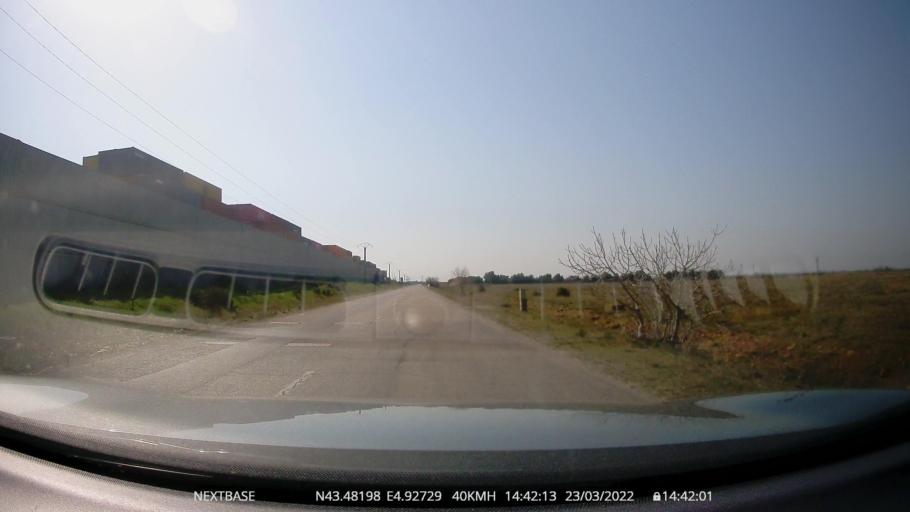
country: FR
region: Provence-Alpes-Cote d'Azur
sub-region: Departement des Bouches-du-Rhone
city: Fos-sur-Mer
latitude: 43.4821
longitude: 4.9283
